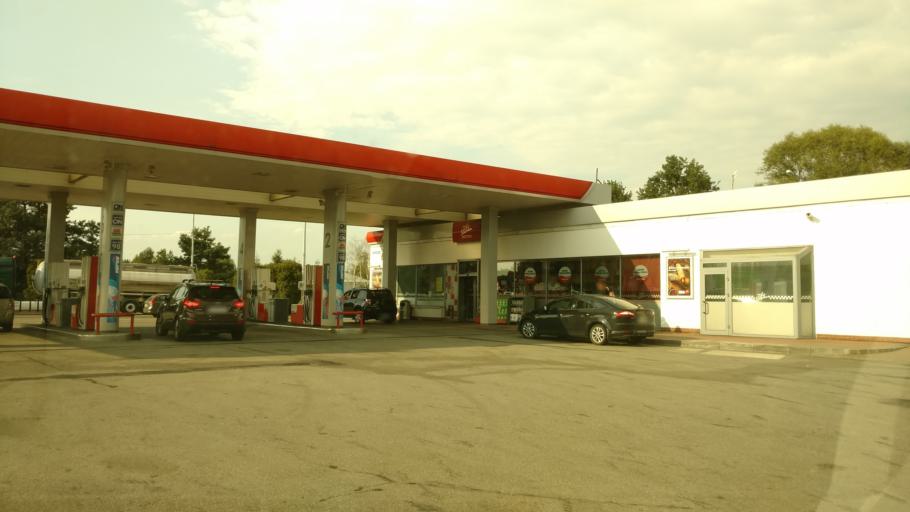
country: PL
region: Silesian Voivodeship
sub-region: Powiat pszczynski
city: Pszczyna
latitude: 49.9871
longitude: 18.9555
